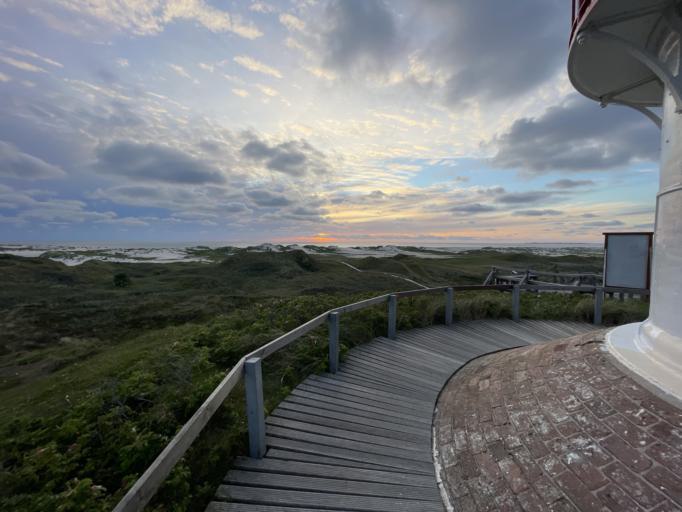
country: DE
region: Schleswig-Holstein
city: Norddorf
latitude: 54.6691
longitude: 8.3085
